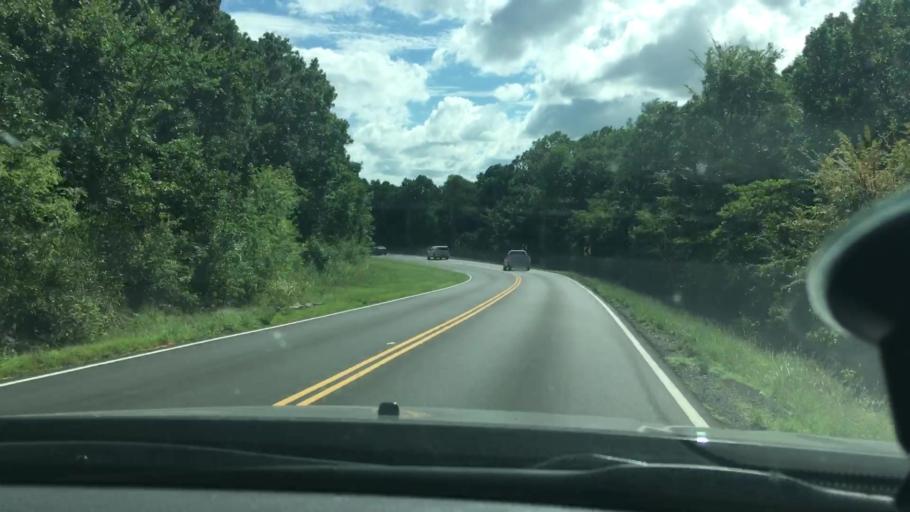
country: US
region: Oklahoma
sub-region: Sequoyah County
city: Vian
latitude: 35.6590
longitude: -94.9512
